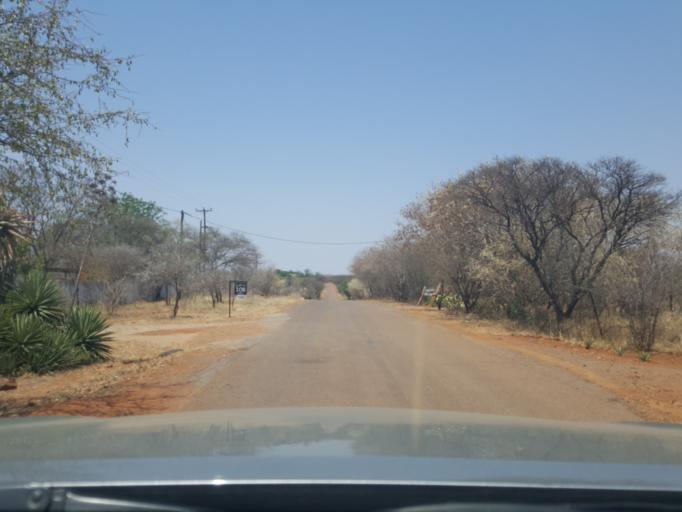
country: BW
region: South East
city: Ramotswa
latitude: -24.7669
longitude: 25.8453
